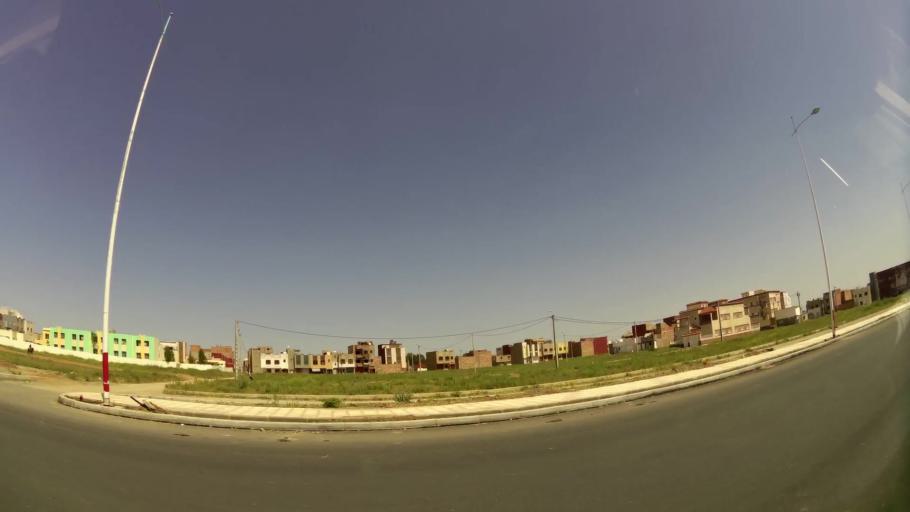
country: MA
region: Rabat-Sale-Zemmour-Zaer
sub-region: Khemisset
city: Khemisset
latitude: 33.8074
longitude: -6.0831
